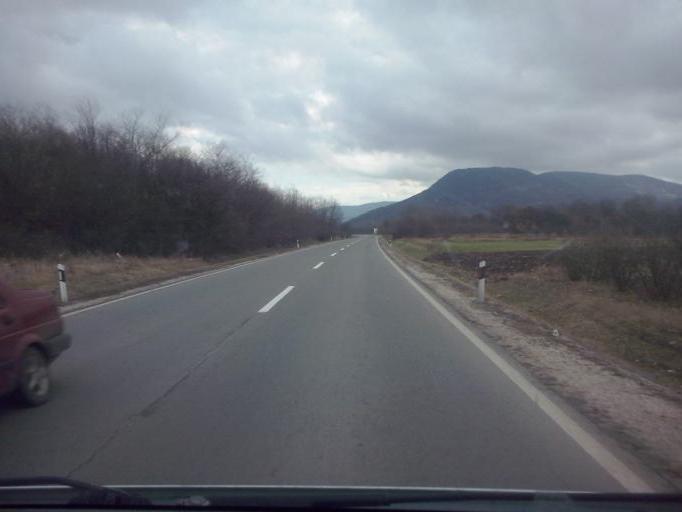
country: RS
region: Central Serbia
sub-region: Pomoravski Okrug
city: Paracin
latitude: 43.8655
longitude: 21.4962
